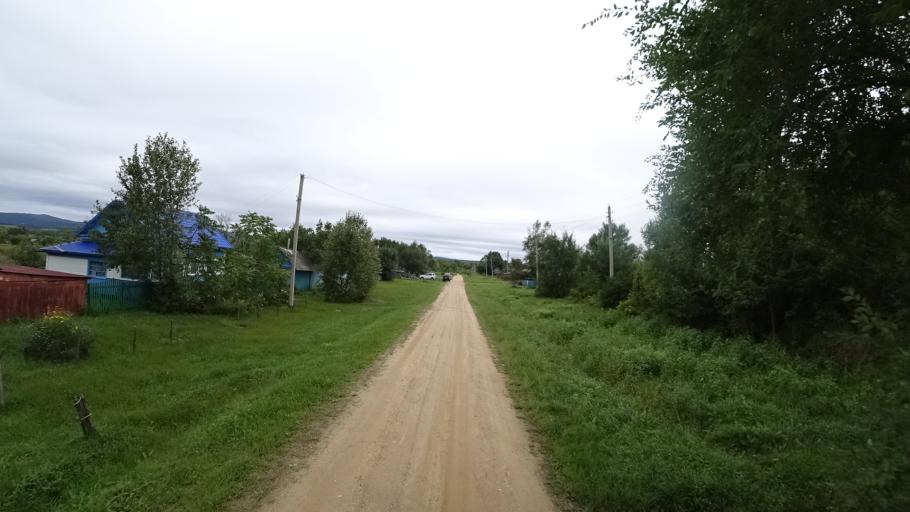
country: RU
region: Primorskiy
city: Rettikhovka
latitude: 44.1403
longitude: 132.6369
